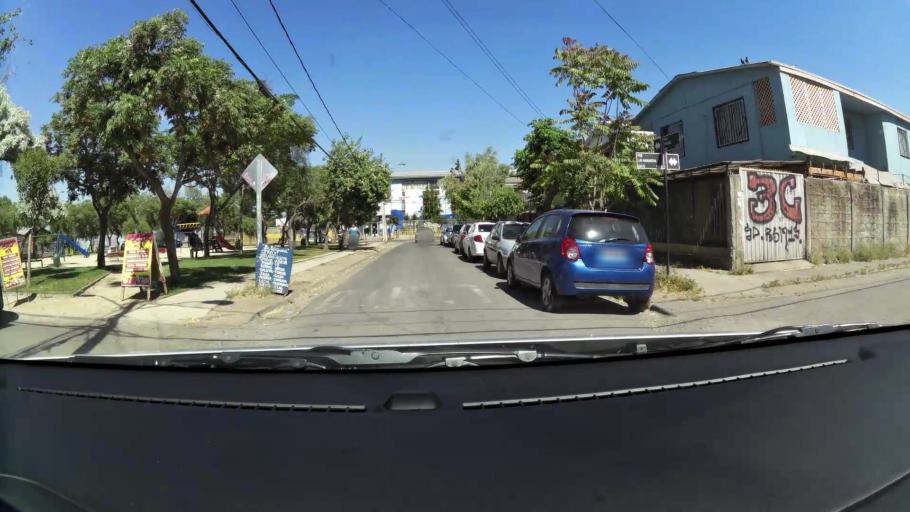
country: CL
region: Santiago Metropolitan
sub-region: Provincia de Santiago
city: La Pintana
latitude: -33.5599
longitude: -70.6574
